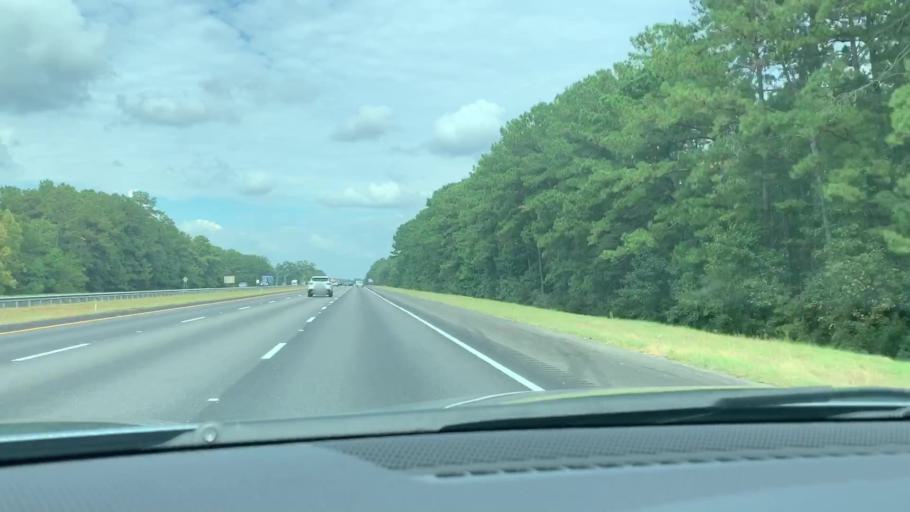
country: US
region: Georgia
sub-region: Chatham County
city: Port Wentworth
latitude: 32.2087
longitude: -81.1800
